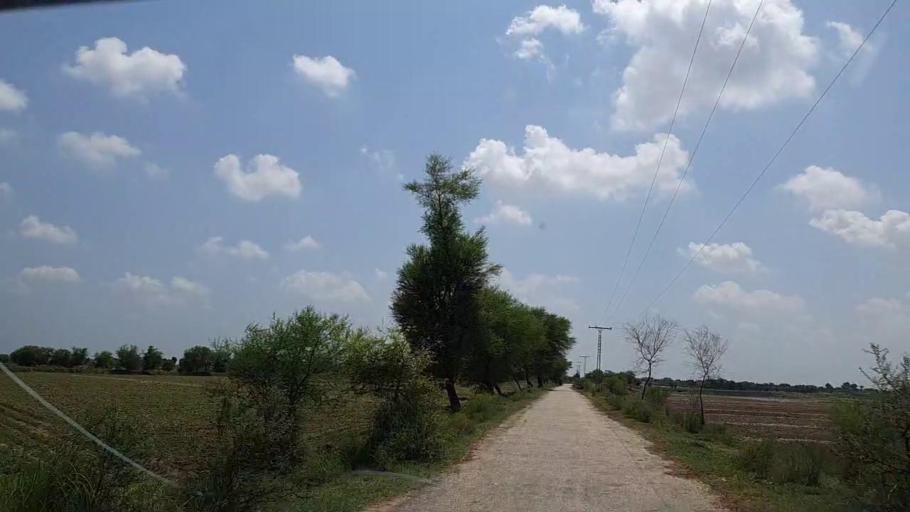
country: PK
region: Sindh
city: Tharu Shah
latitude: 27.0075
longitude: 68.0642
